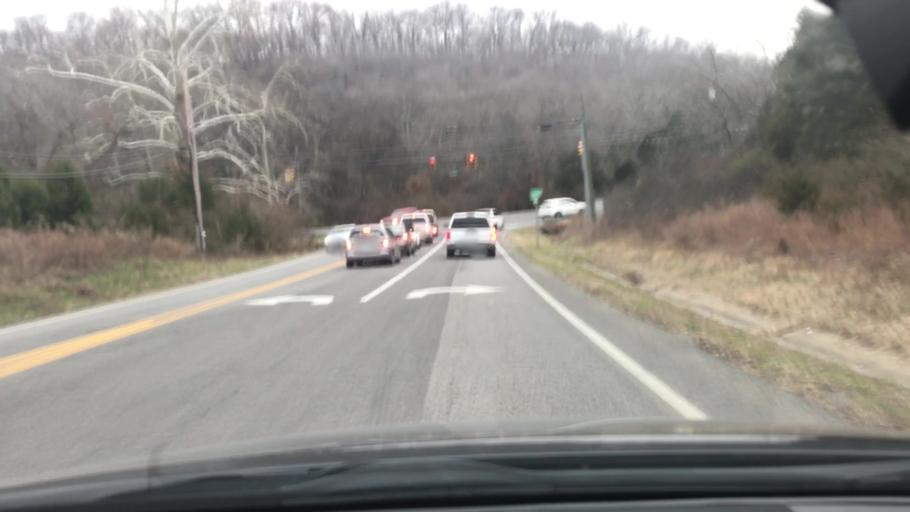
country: US
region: Tennessee
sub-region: Davidson County
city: Forest Hills
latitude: 36.0310
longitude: -86.8747
